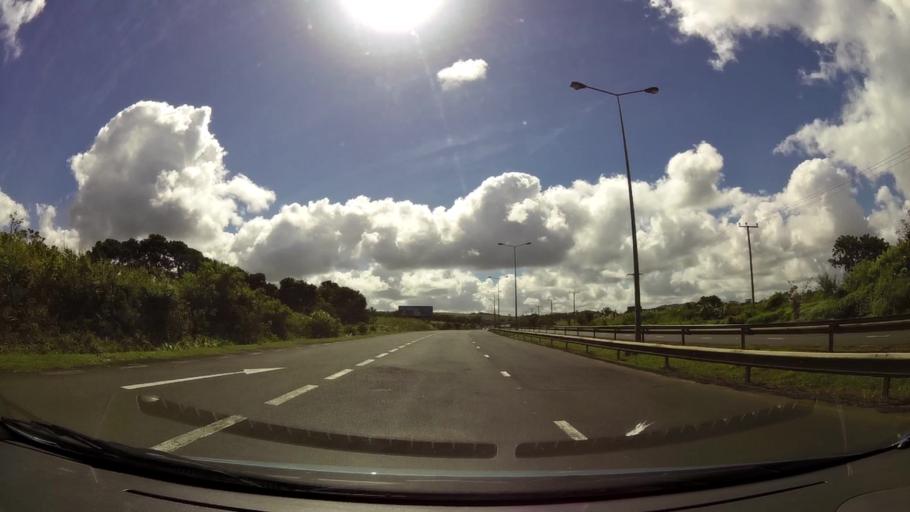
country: MU
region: Grand Port
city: Nouvelle France
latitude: -20.3833
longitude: 57.5727
